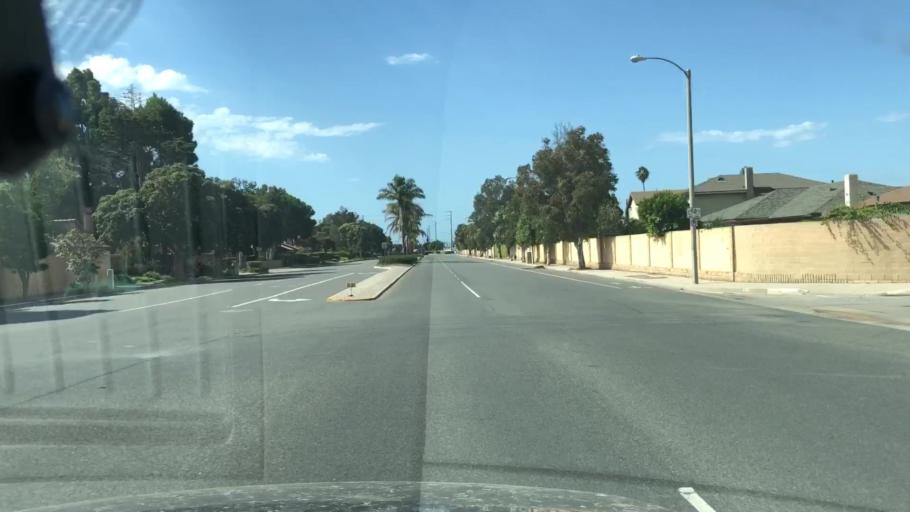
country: US
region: California
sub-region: Ventura County
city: Oxnard Shores
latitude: 34.1904
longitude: -119.2173
